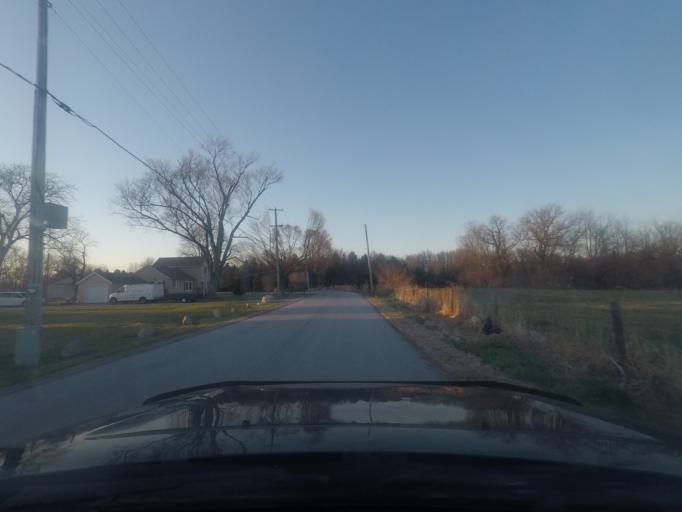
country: US
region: Indiana
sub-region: LaPorte County
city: Kingsford Heights
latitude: 41.5123
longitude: -86.6977
